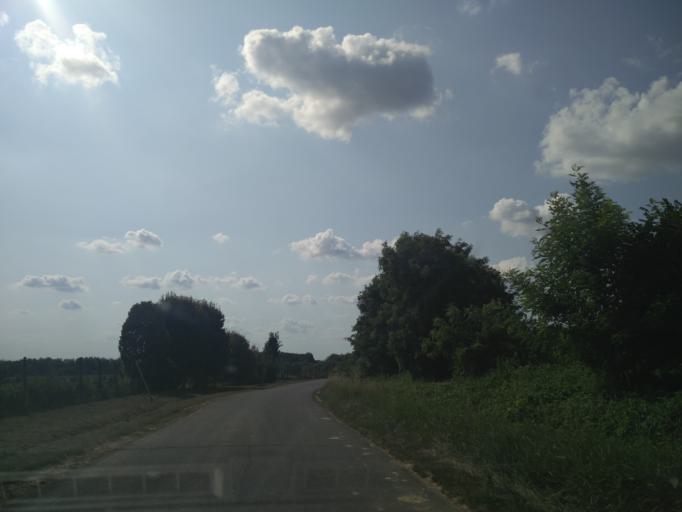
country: HU
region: Zala
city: Zalaegerszeg
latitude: 46.8965
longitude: 16.7879
